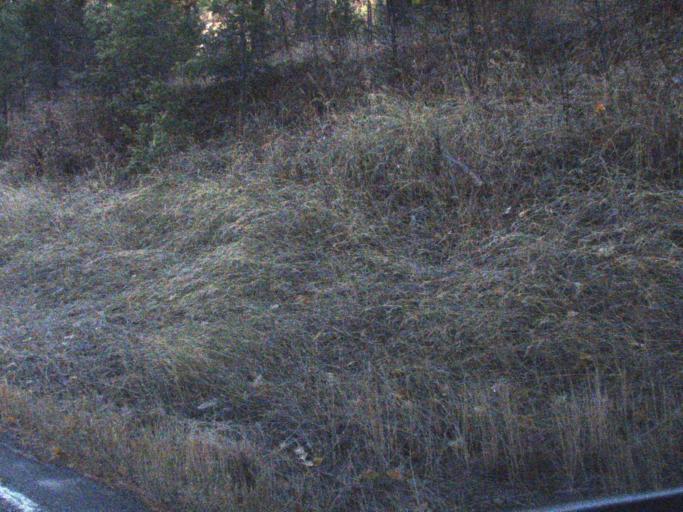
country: US
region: Washington
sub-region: Ferry County
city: Republic
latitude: 48.2885
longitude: -118.7286
